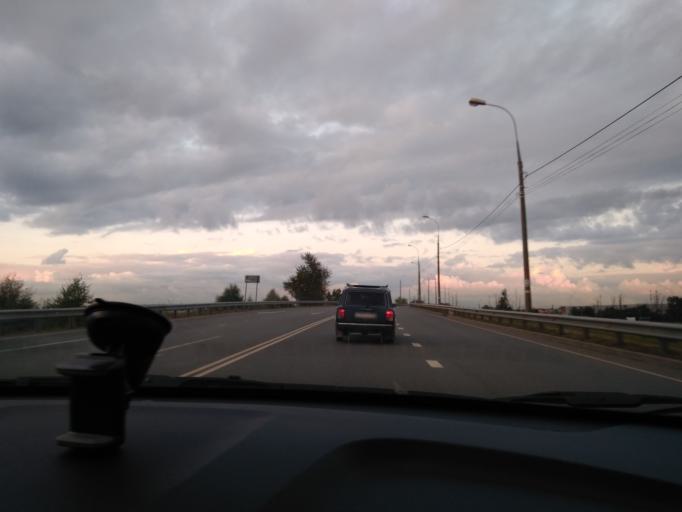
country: RU
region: Moskovskaya
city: Ramenskoye
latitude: 55.4878
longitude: 38.1550
